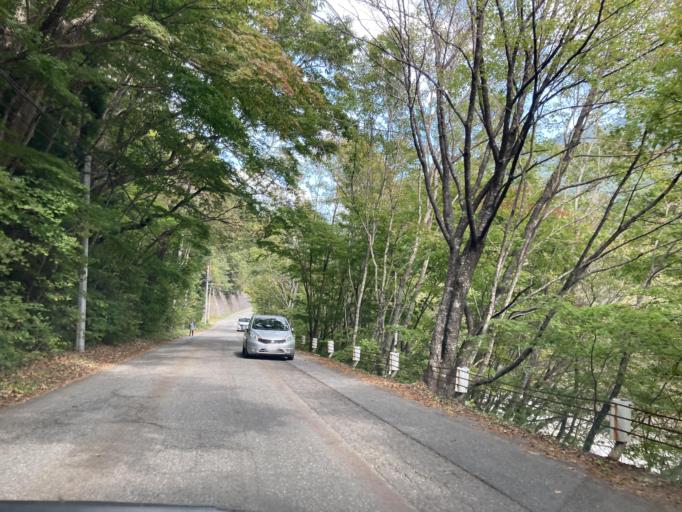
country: JP
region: Nagano
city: Omachi
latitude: 36.4916
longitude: 137.7448
